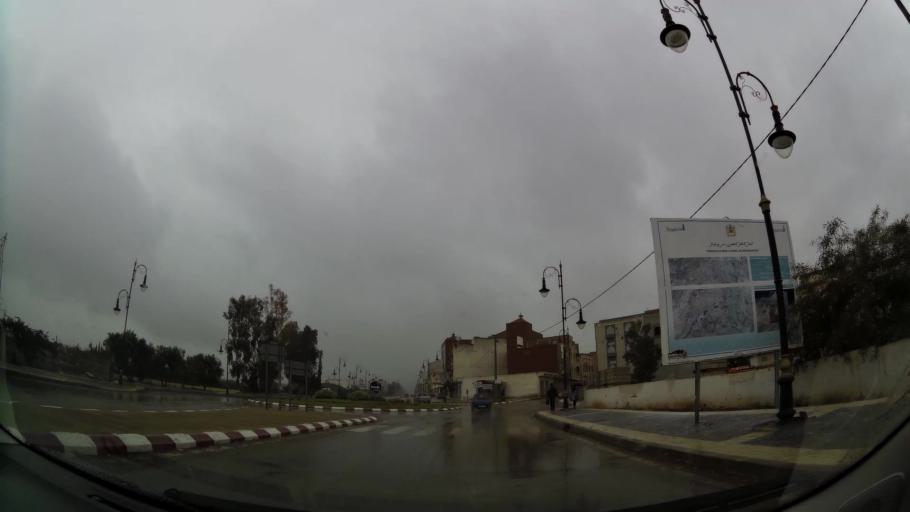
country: MA
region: Taza-Al Hoceima-Taounate
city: Imzourene
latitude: 35.1152
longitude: -3.8419
